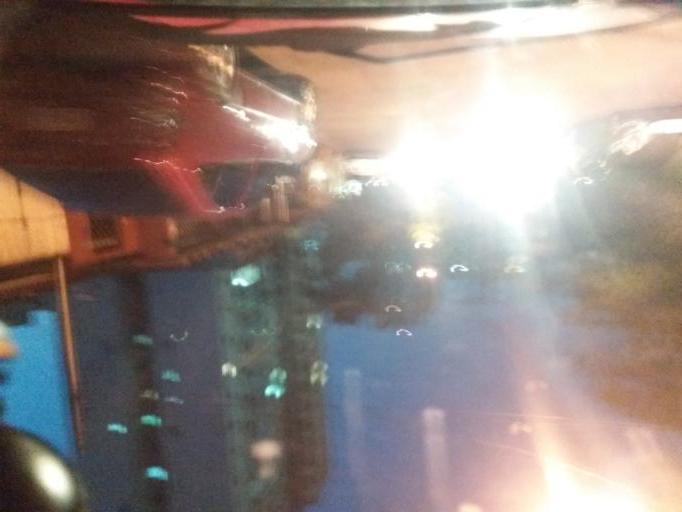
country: BR
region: Sao Paulo
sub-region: Taboao Da Serra
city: Taboao da Serra
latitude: -23.6224
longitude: -46.7442
